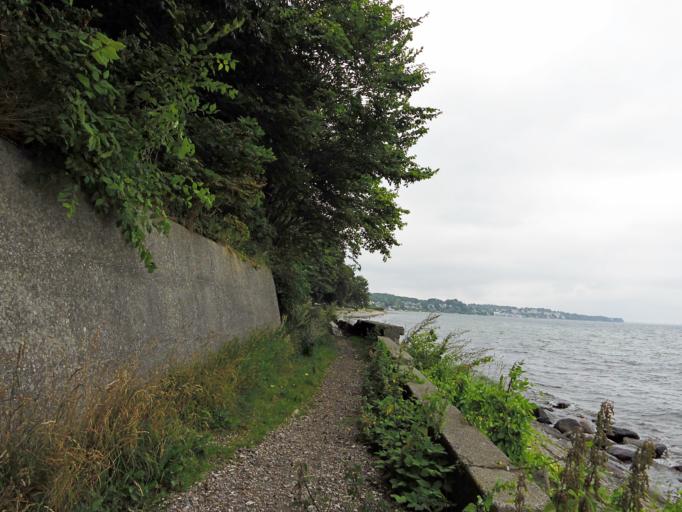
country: DK
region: Capital Region
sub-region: Gentofte Kommune
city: Charlottenlund
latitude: 55.8051
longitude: 12.5857
